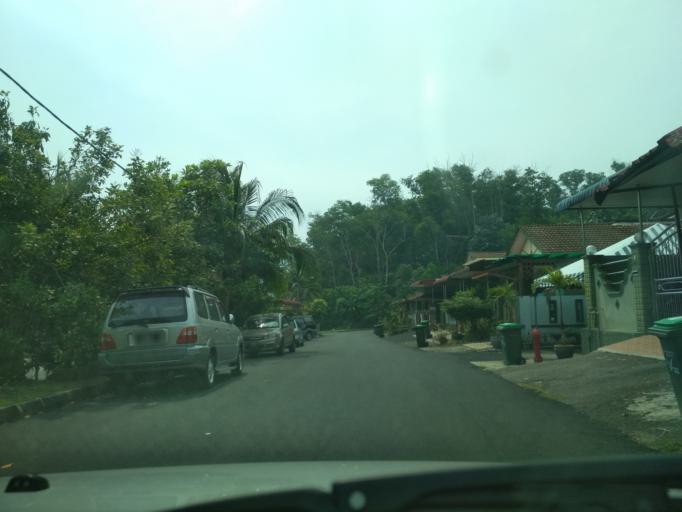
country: MY
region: Kedah
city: Kulim
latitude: 5.3707
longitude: 100.5679
